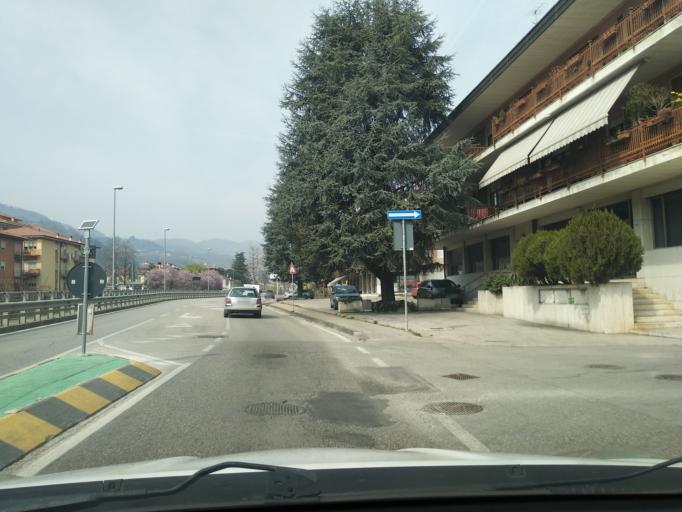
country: IT
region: Veneto
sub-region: Provincia di Vicenza
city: Chiampo
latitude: 45.5460
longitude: 11.2809
